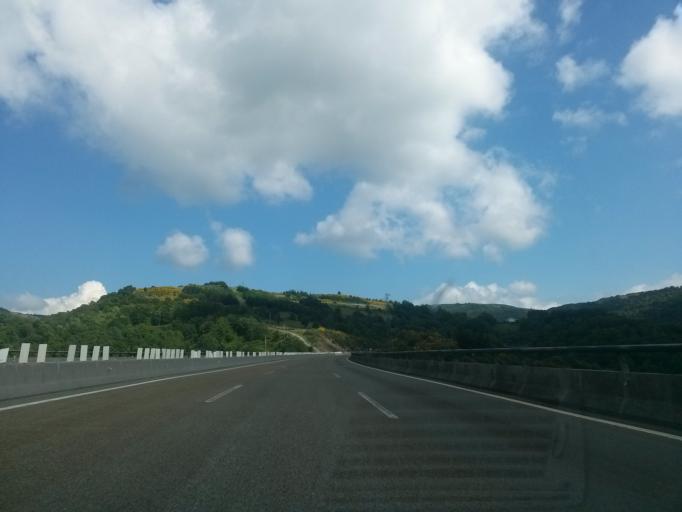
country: ES
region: Galicia
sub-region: Provincia de Lugo
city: San Roman
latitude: 42.7431
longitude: -7.0514
